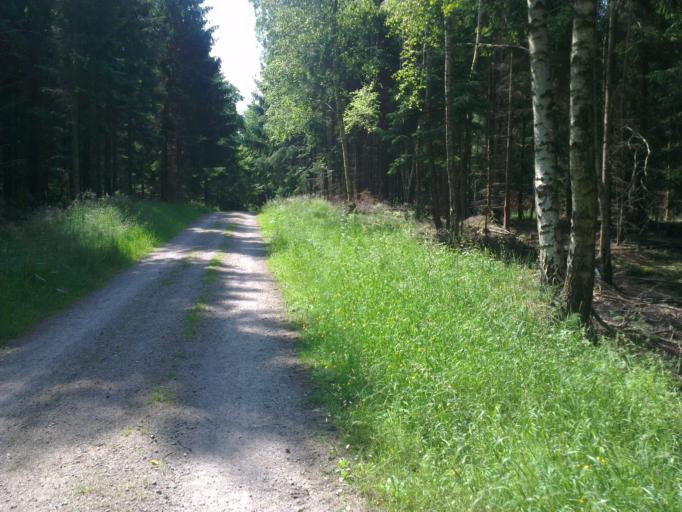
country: DK
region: Capital Region
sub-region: Allerod Kommune
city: Lillerod
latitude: 55.9243
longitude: 12.3616
